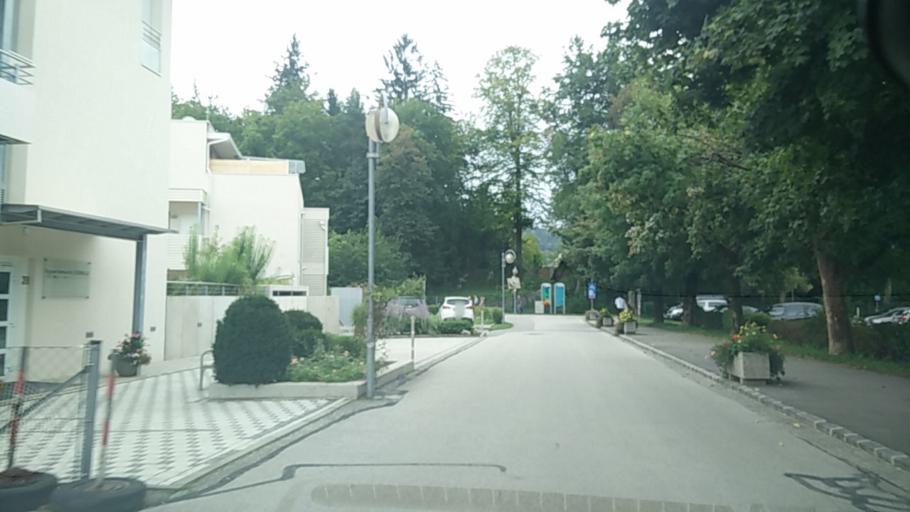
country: AT
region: Carinthia
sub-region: Politischer Bezirk Klagenfurt Land
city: Keutschach am See
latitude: 46.6223
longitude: 14.2140
